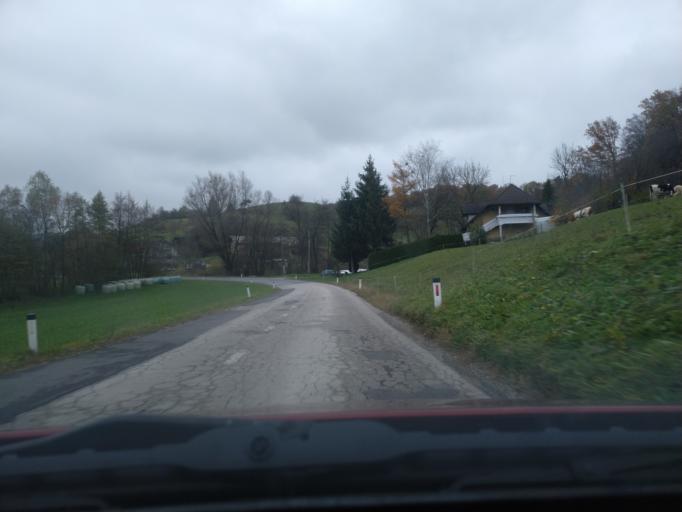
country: SI
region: Kungota
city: Zgornja Kungota
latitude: 46.6551
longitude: 15.6132
